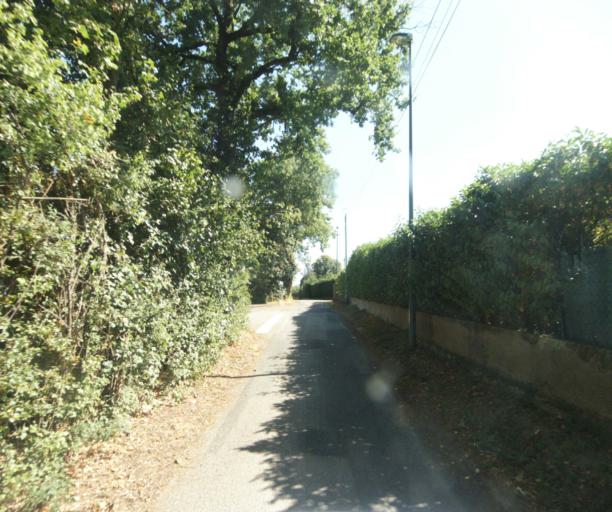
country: FR
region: Rhone-Alpes
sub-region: Departement du Rhone
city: La Tour-de-Salvagny
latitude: 45.8344
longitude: 4.7099
